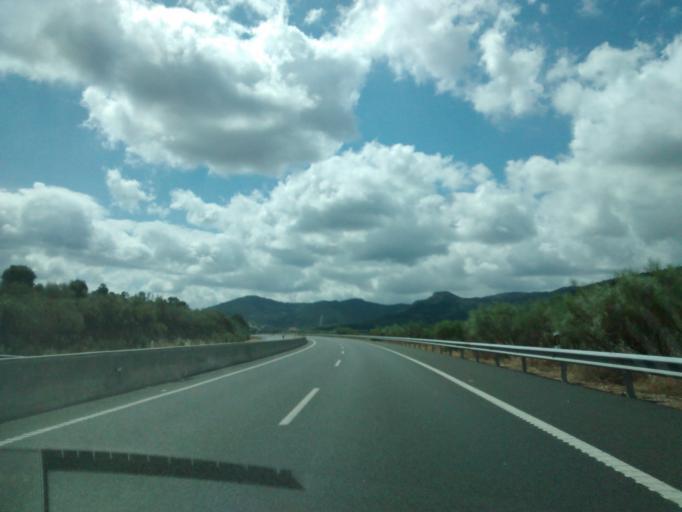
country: ES
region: Extremadura
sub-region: Provincia de Caceres
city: Romangordo
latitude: 39.7183
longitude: -5.7090
